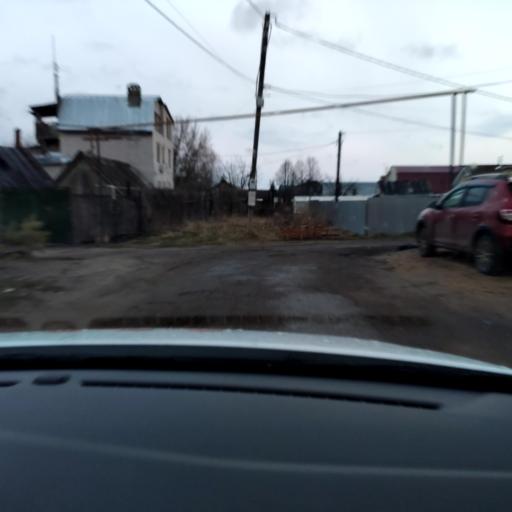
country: RU
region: Tatarstan
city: Stolbishchi
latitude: 55.6956
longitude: 49.1578
